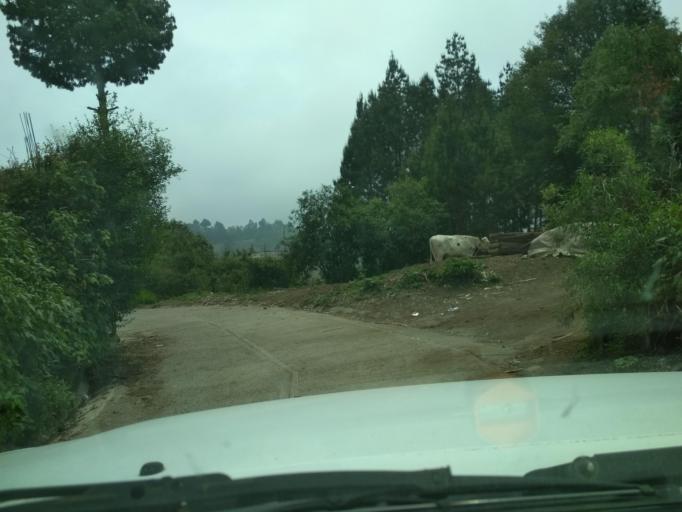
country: MX
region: Veracruz
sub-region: Mariano Escobedo
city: San Isidro el Berro
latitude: 18.9768
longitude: -97.2046
